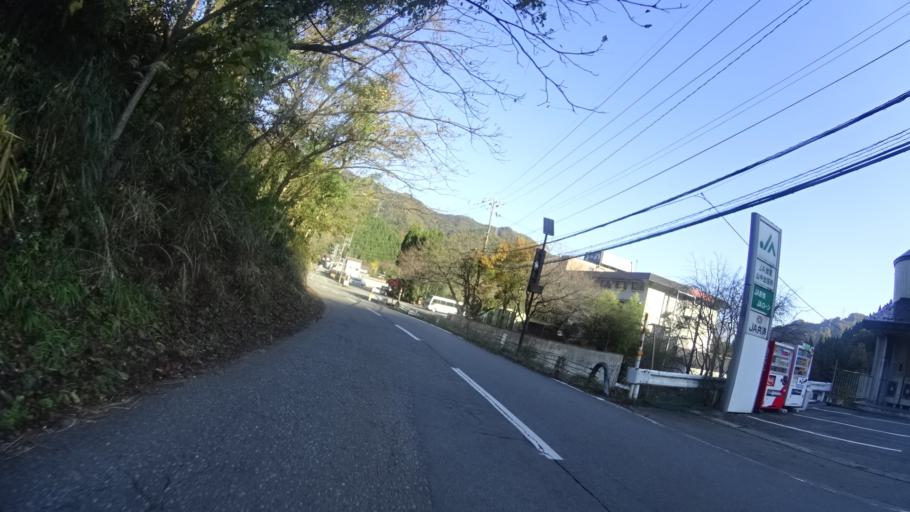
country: JP
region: Fukui
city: Maruoka
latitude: 36.2259
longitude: 136.3608
